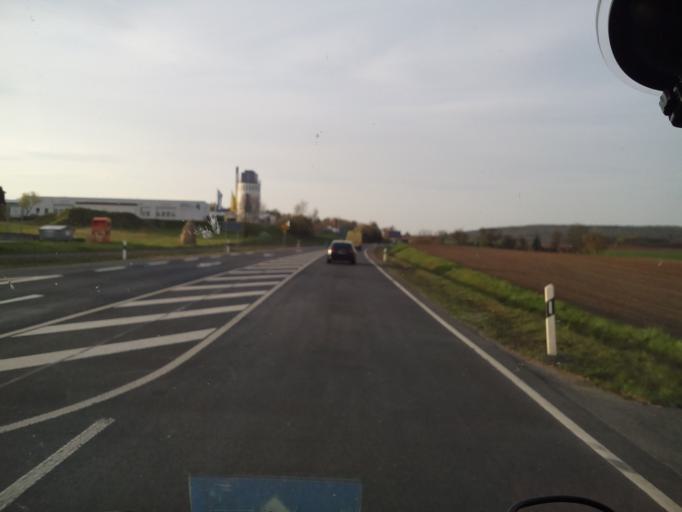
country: DE
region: Bavaria
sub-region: Upper Franconia
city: Reckendorf
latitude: 50.0228
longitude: 10.8265
